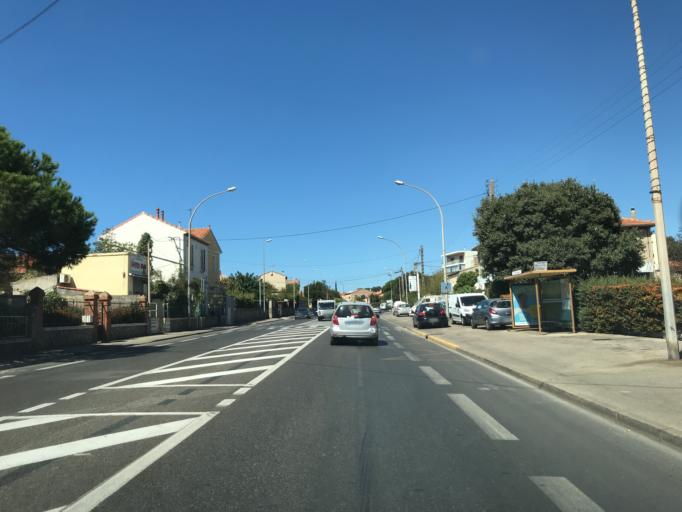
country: FR
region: Provence-Alpes-Cote d'Azur
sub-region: Departement du Var
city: La Seyne-sur-Mer
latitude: 43.0817
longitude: 5.8841
